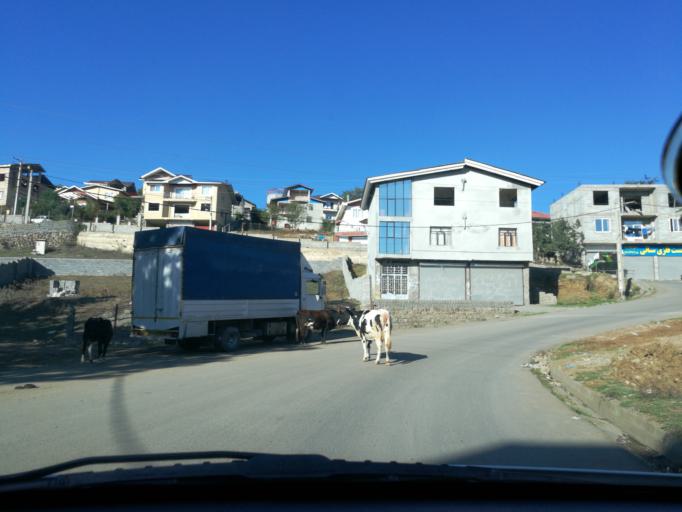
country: IR
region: Mazandaran
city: `Abbasabad
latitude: 36.5500
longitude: 51.1896
